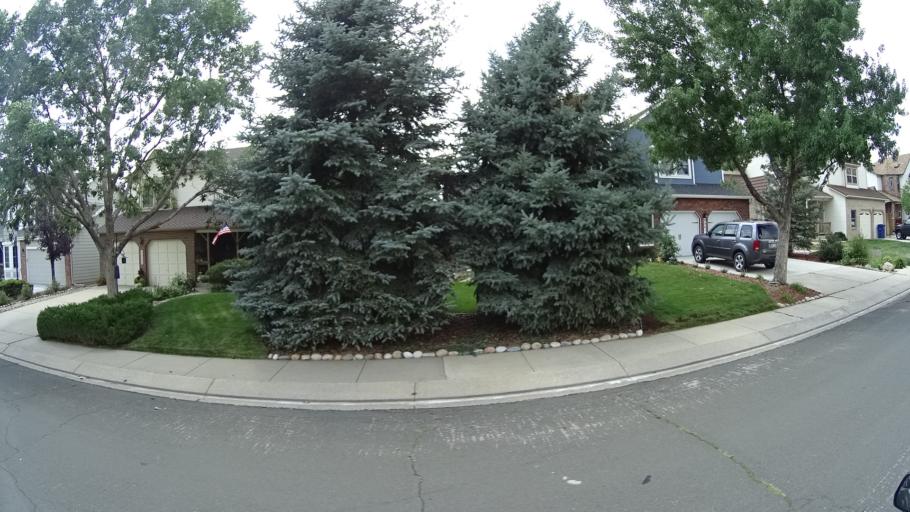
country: US
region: Colorado
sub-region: El Paso County
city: Black Forest
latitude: 38.9582
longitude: -104.7442
